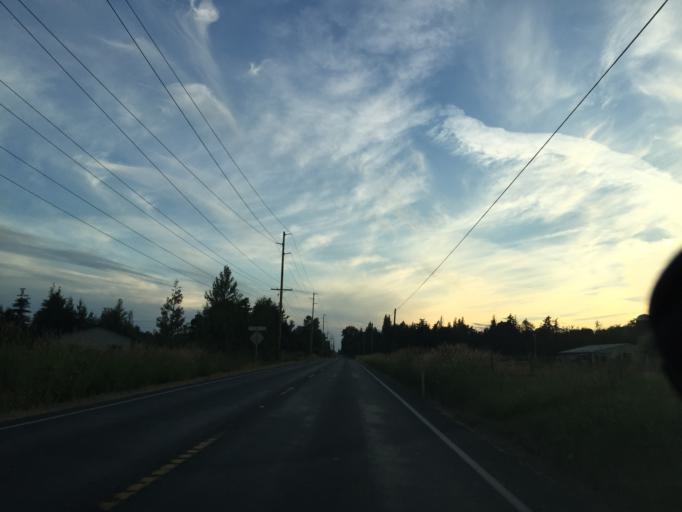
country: US
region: Washington
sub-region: Whatcom County
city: Everson
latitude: 48.9637
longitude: -122.3545
